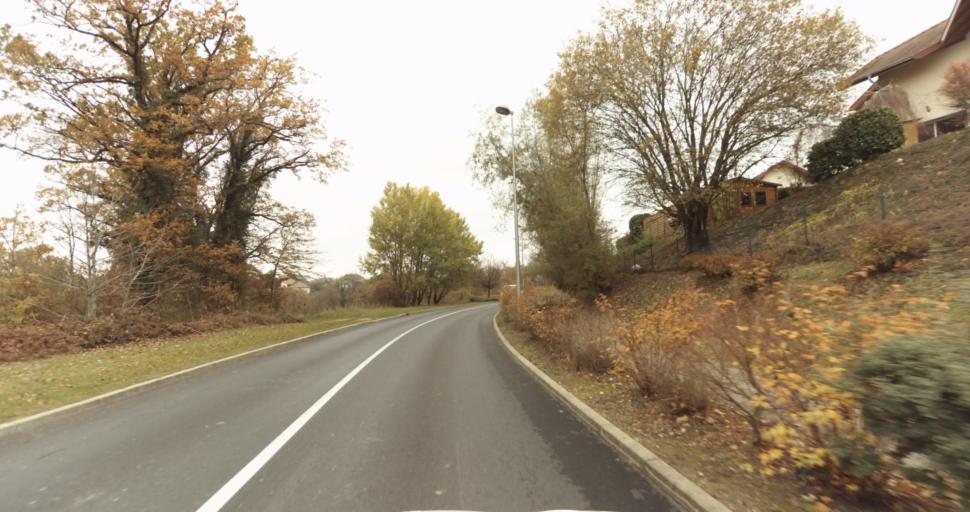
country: FR
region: Rhone-Alpes
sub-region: Departement de la Haute-Savoie
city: Seynod
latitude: 45.8606
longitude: 6.0787
